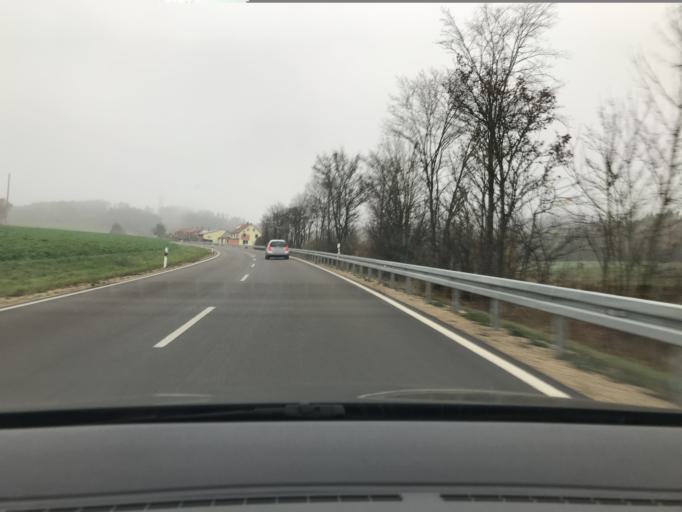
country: DE
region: Bavaria
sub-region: Swabia
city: Fremdingen
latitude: 48.9868
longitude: 10.4320
